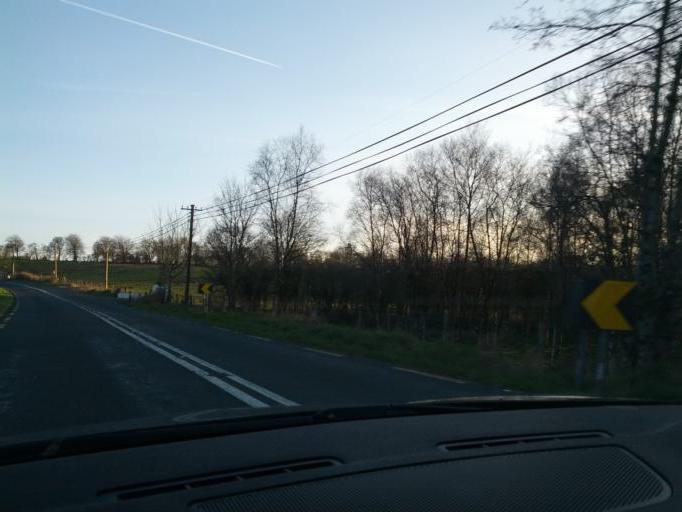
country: IE
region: Connaught
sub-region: Sligo
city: Tobercurry
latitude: 54.0865
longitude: -8.7037
